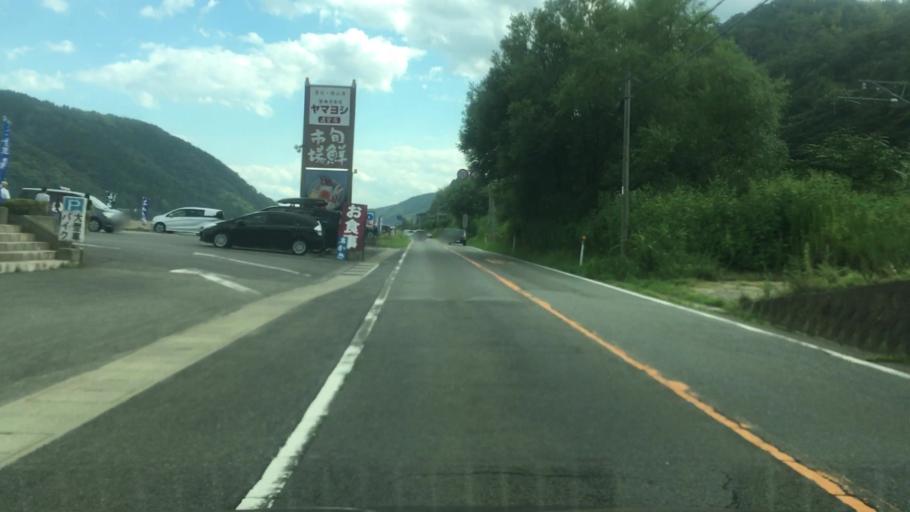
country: JP
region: Hyogo
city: Toyooka
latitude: 35.6034
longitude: 134.8017
